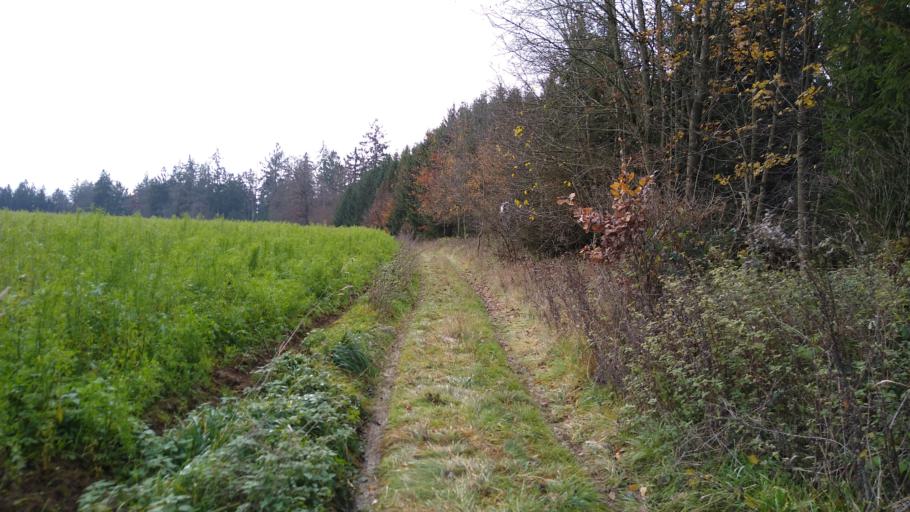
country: DE
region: Bavaria
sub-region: Upper Palatinate
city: Seubersdorf
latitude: 49.1488
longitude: 11.6352
